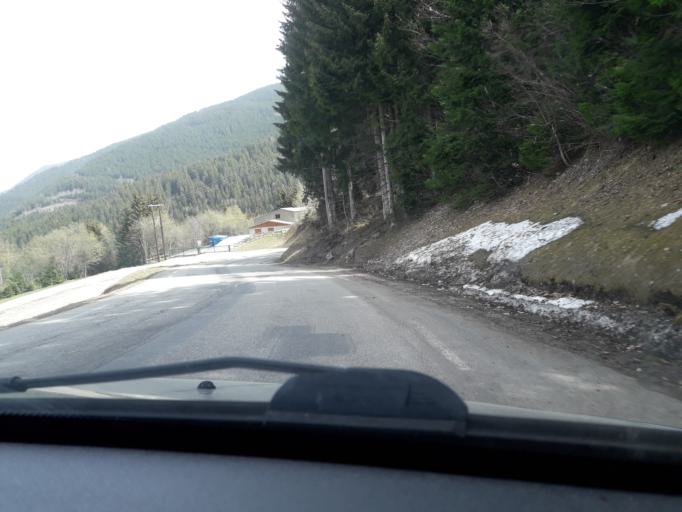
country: FR
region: Rhone-Alpes
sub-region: Departement de l'Isere
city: Theys
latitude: 45.2580
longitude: 5.9962
